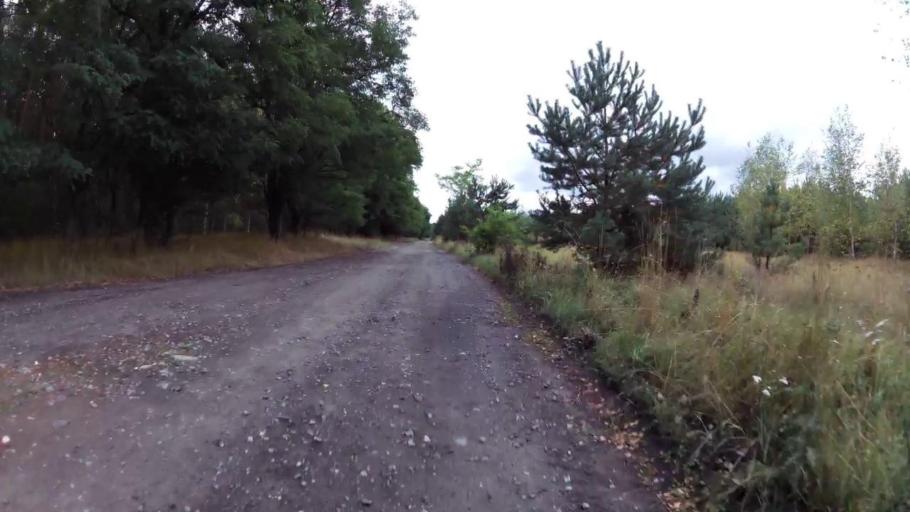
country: PL
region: West Pomeranian Voivodeship
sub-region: Powiat mysliborski
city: Debno
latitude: 52.8609
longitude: 14.7179
